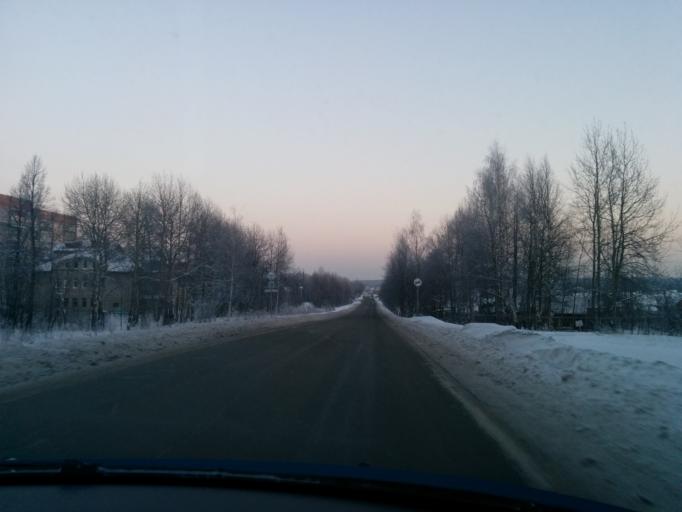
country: RU
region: Perm
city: Novyye Lyady
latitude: 58.0473
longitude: 56.5799
